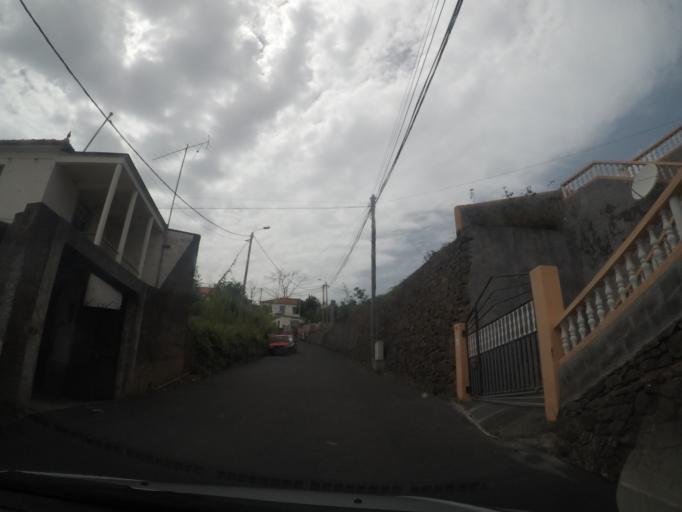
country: PT
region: Madeira
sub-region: Santa Cruz
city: Santa Cruz
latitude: 32.6889
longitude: -16.8115
